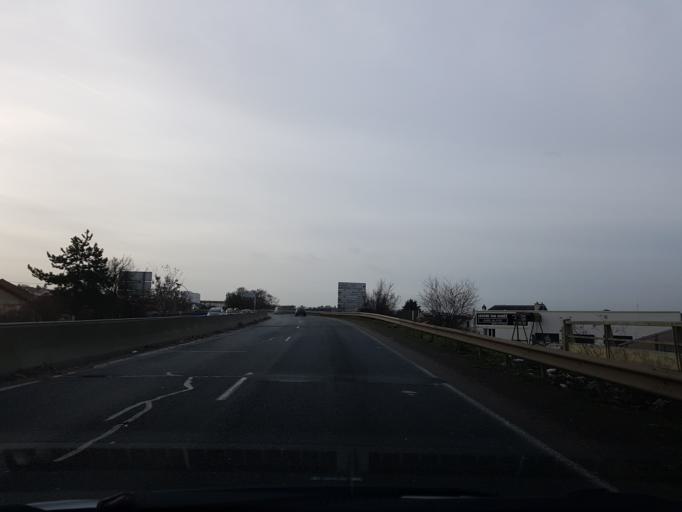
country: FR
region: Ile-de-France
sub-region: Departement de l'Essonne
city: Montgeron
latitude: 48.7112
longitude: 2.4418
